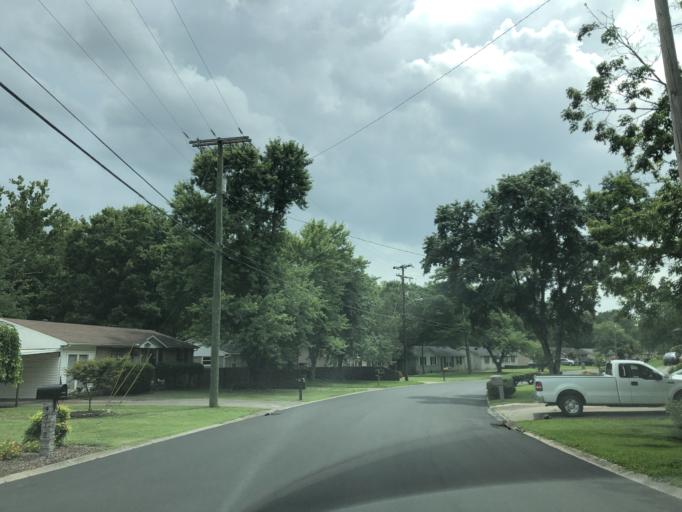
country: US
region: Tennessee
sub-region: Williamson County
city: Nolensville
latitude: 36.0553
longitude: -86.6775
